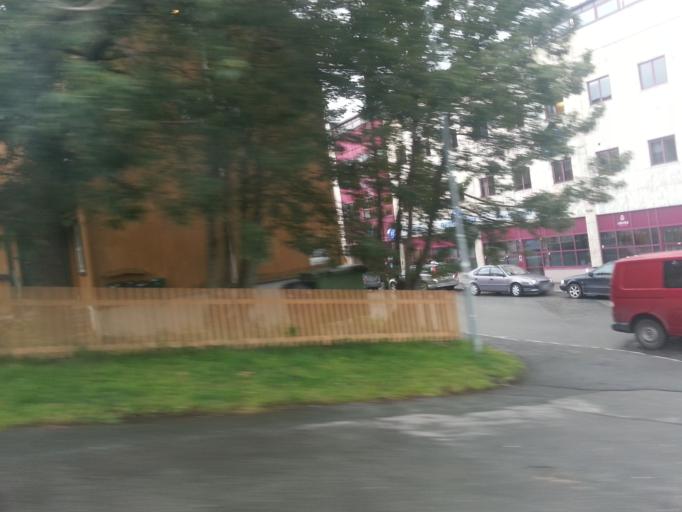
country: NO
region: Troms
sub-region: Tromso
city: Tromso
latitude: 69.6500
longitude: 18.9525
